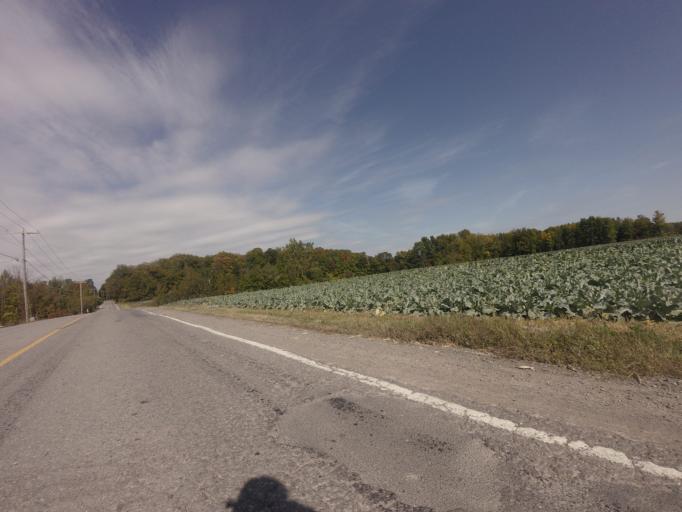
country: CA
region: Quebec
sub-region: Laurentides
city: Saint-Eustache
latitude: 45.6019
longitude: -73.9164
